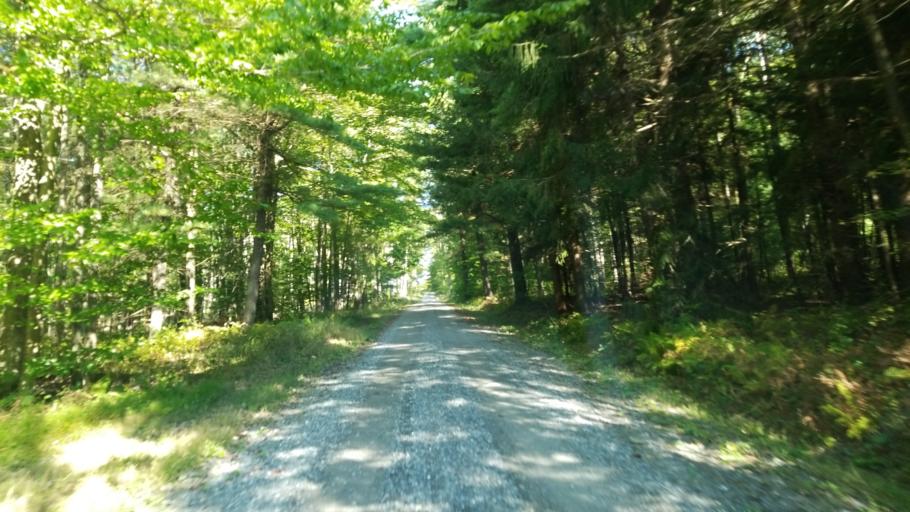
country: US
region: Pennsylvania
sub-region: Clearfield County
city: Treasure Lake
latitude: 41.1378
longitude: -78.5718
